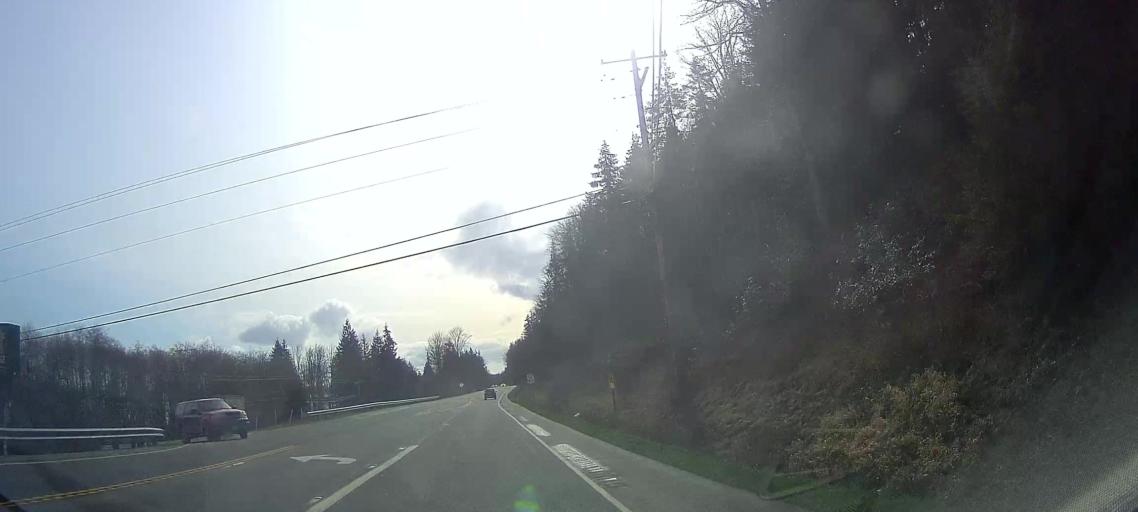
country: US
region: Washington
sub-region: Island County
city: Camano
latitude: 48.2074
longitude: -122.4793
